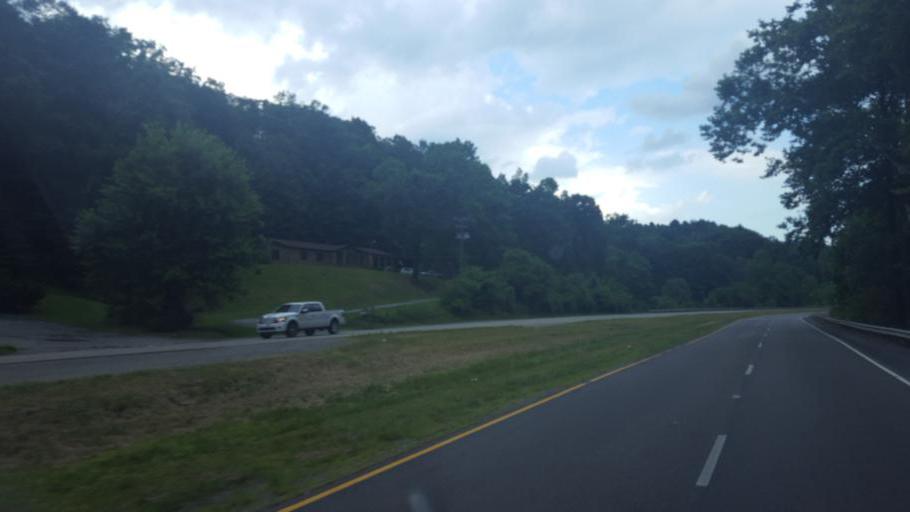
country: US
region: Virginia
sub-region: Wise County
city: Pound
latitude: 37.0880
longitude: -82.5994
